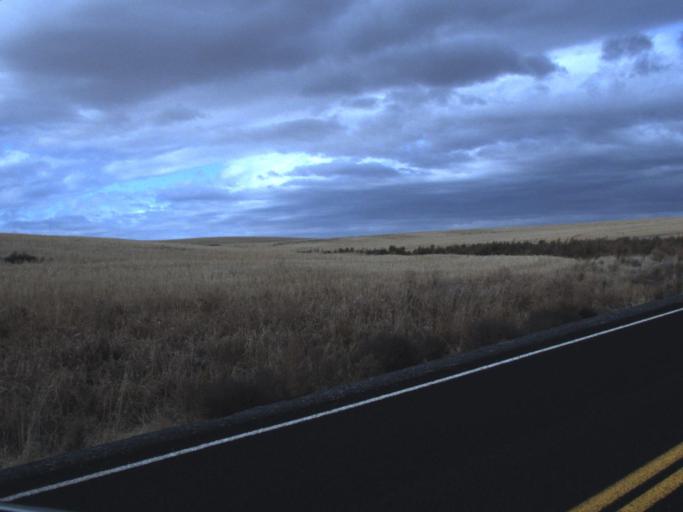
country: US
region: Washington
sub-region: Okanogan County
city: Coulee Dam
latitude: 47.8593
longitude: -118.7211
